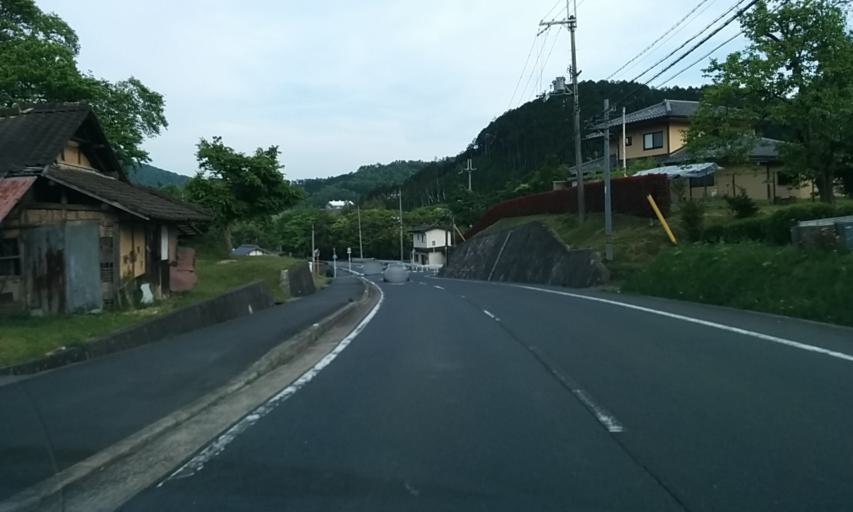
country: JP
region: Kyoto
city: Ayabe
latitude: 35.1612
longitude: 135.4090
